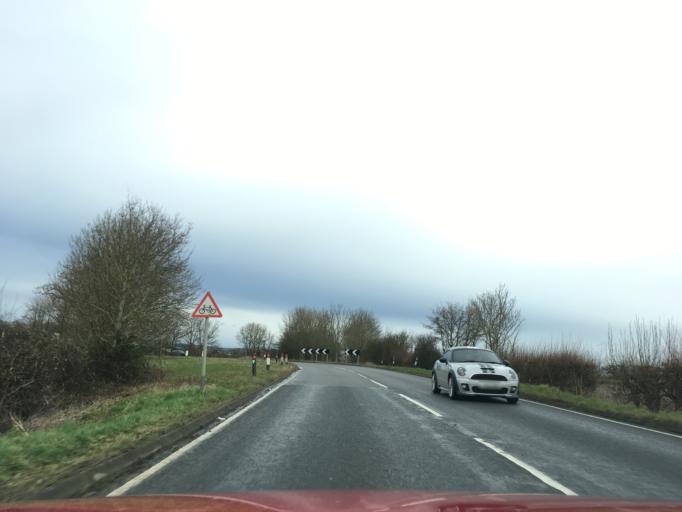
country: GB
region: England
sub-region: Worcestershire
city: Evesham
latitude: 52.0534
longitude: -1.9601
